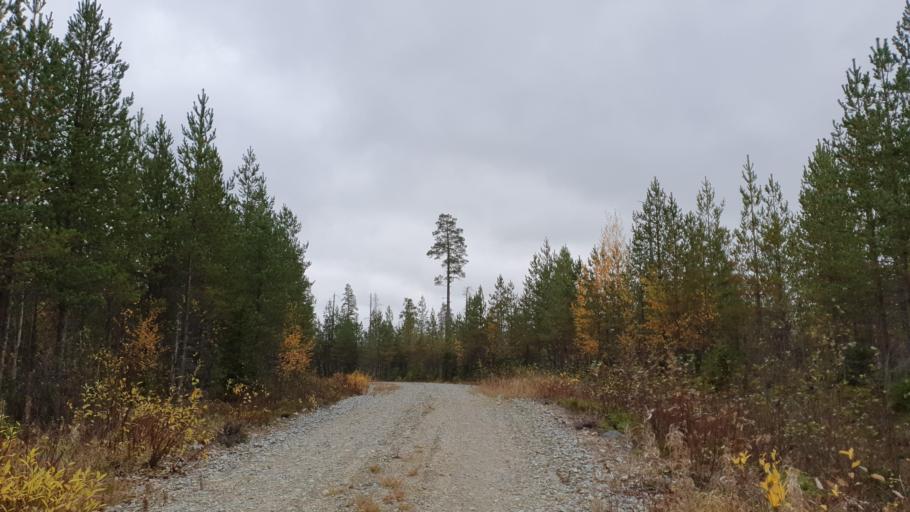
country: FI
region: Kainuu
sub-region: Kehys-Kainuu
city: Kuhmo
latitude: 64.4491
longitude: 29.5992
